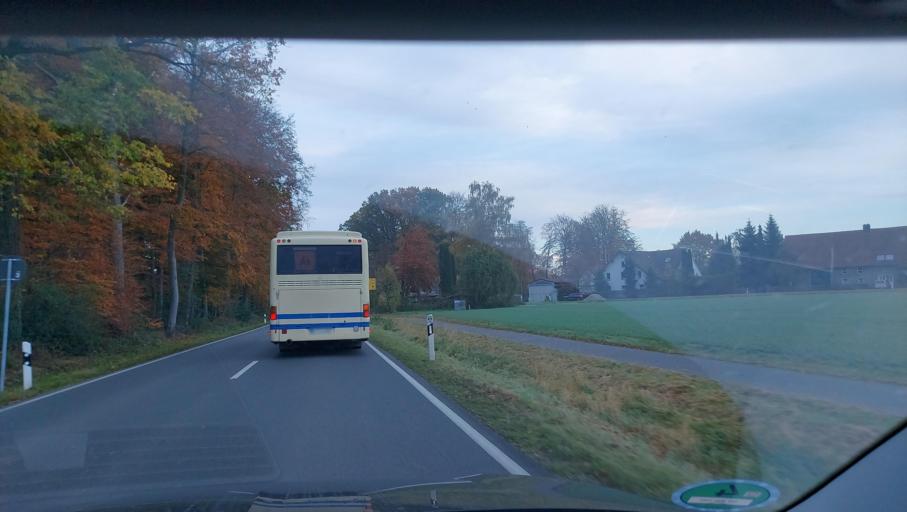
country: DE
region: Lower Saxony
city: Neuenkirchen
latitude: 52.1025
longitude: 8.3712
